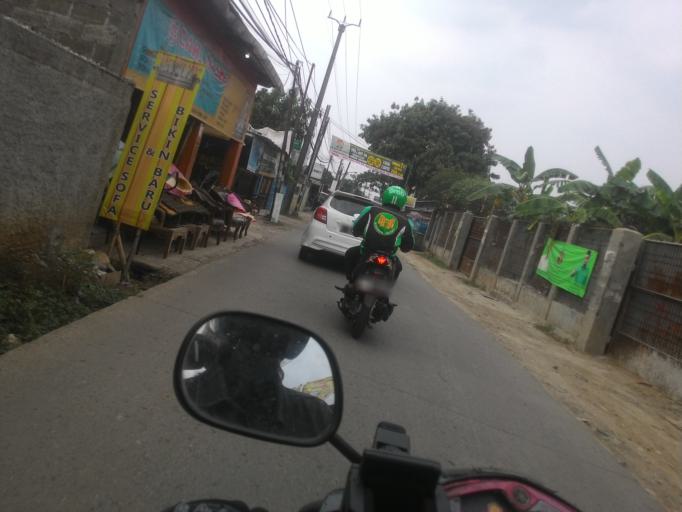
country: ID
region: West Java
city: Depok
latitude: -6.4270
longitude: 106.8369
